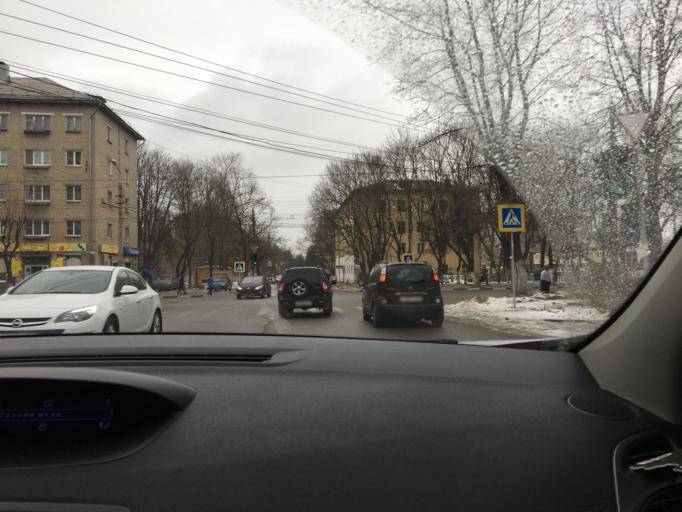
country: RU
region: Tula
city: Mendeleyevskiy
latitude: 54.1642
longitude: 37.5821
